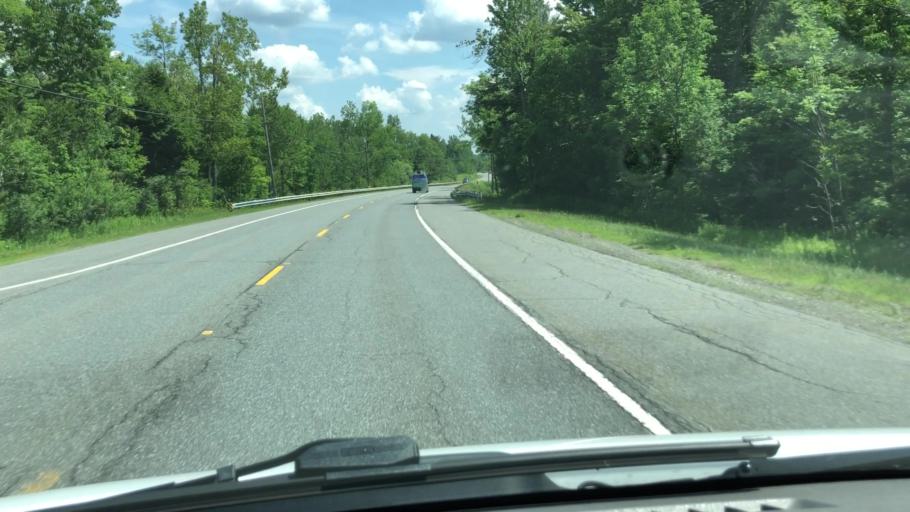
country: US
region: Massachusetts
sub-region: Berkshire County
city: Hinsdale
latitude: 42.5063
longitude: -73.0401
